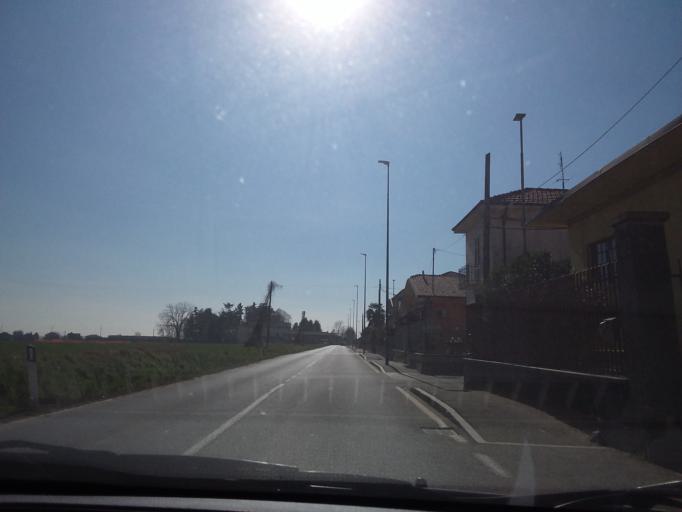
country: IT
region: Piedmont
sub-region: Provincia di Torino
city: Tetti Neirotti
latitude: 45.0561
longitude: 7.5384
